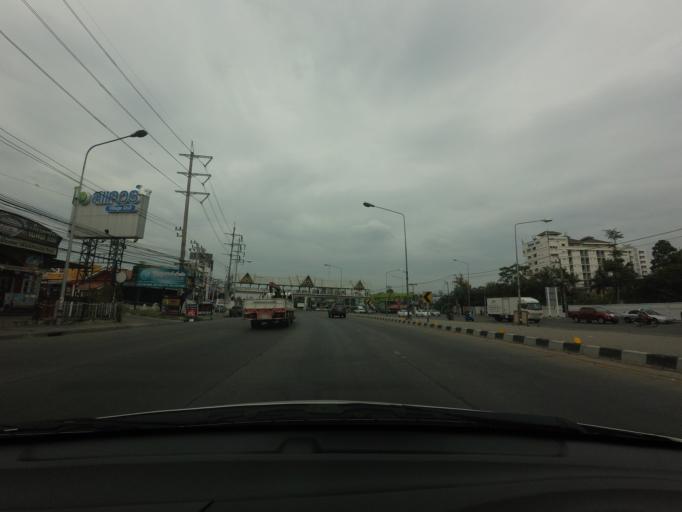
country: TH
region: Samut Prakan
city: Samut Prakan
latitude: 13.5979
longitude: 100.6120
